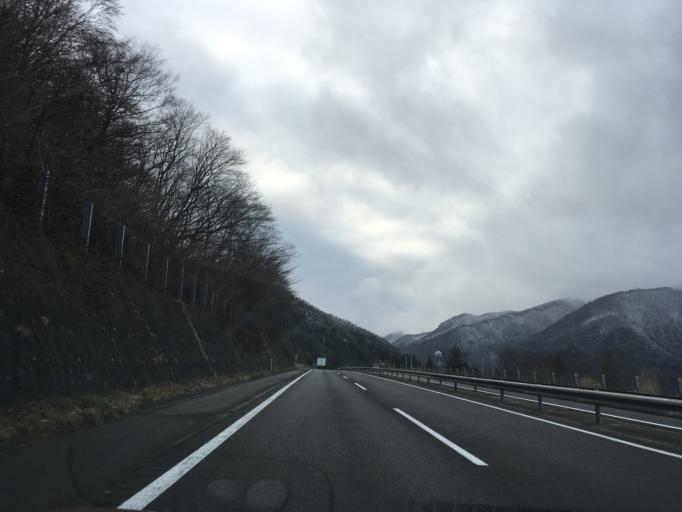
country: JP
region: Miyagi
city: Shiroishi
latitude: 38.1982
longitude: 140.5870
